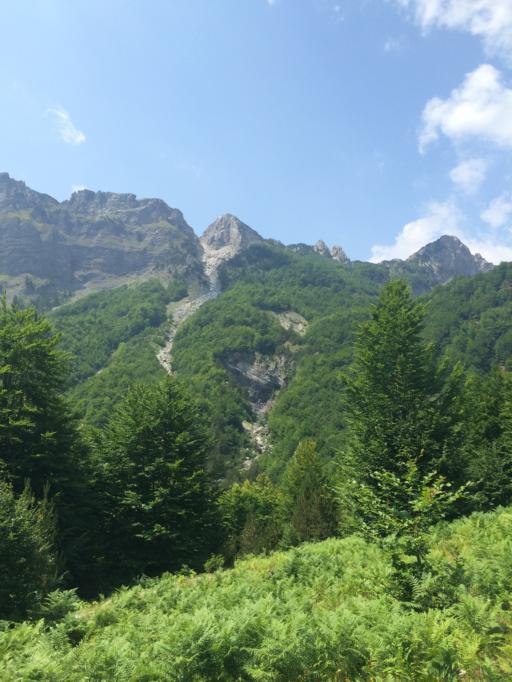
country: AL
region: Kukes
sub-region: Rrethi i Tropojes
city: Valbone
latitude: 42.4106
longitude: 19.8329
